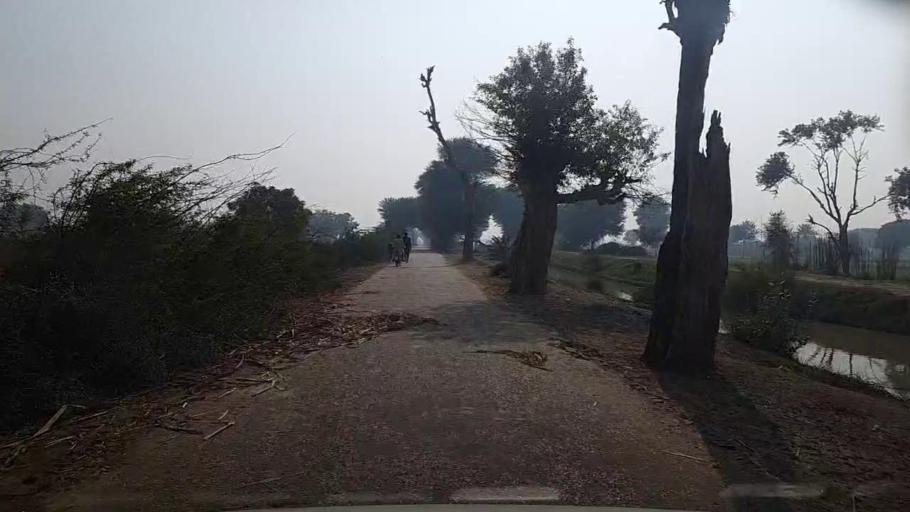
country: PK
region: Sindh
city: Setharja Old
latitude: 27.1143
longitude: 68.5094
